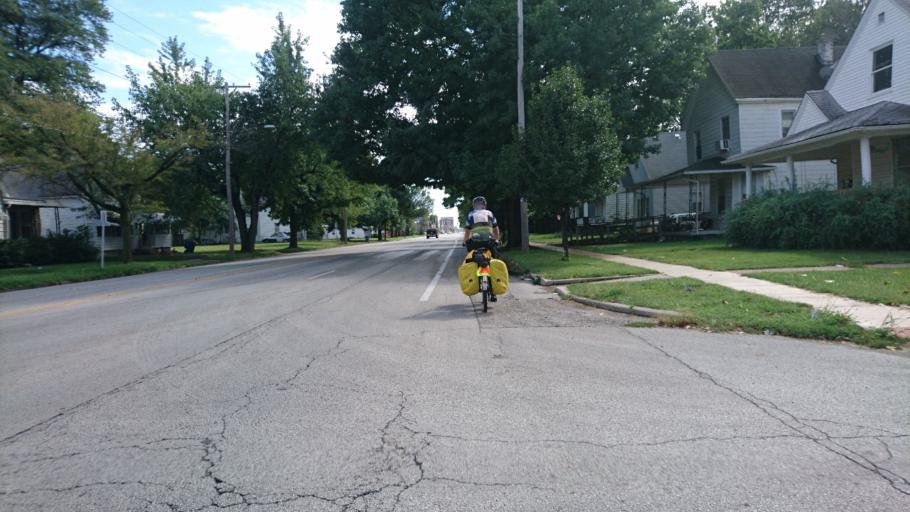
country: US
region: Illinois
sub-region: Sangamon County
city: Springfield
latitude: 39.8127
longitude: -89.6434
